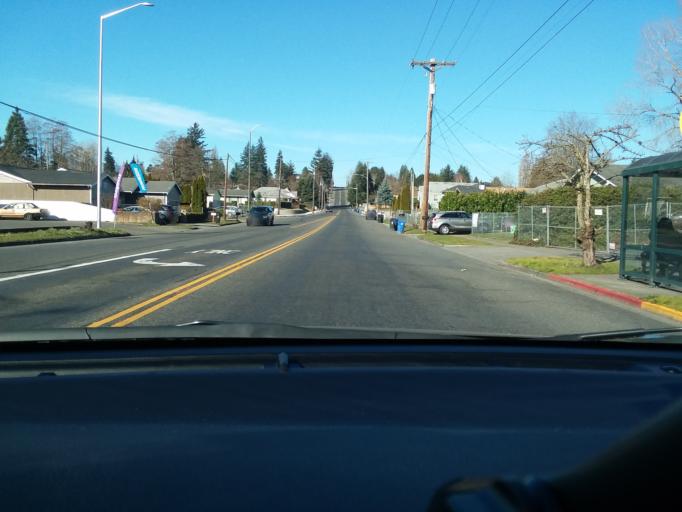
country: US
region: Washington
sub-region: Pierce County
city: Midland
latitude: 47.2062
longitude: -122.4083
